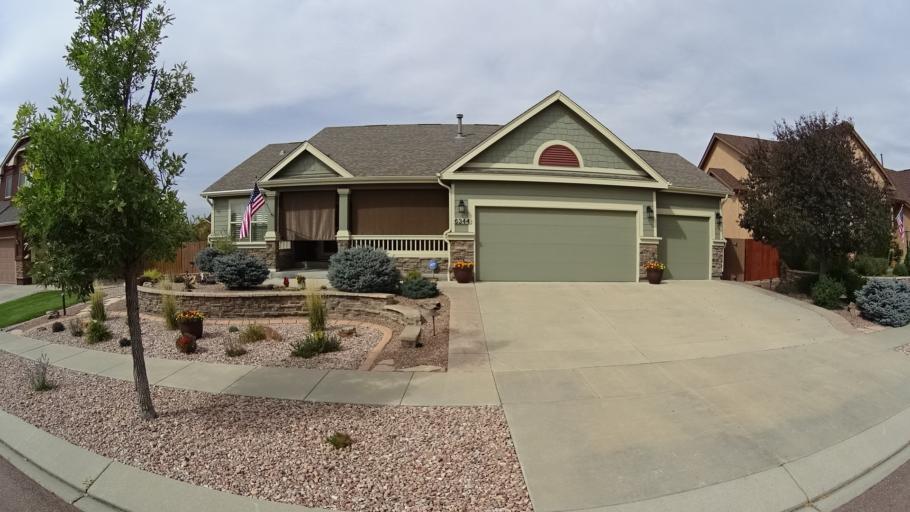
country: US
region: Colorado
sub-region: El Paso County
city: Cimarron Hills
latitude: 38.9236
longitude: -104.6943
